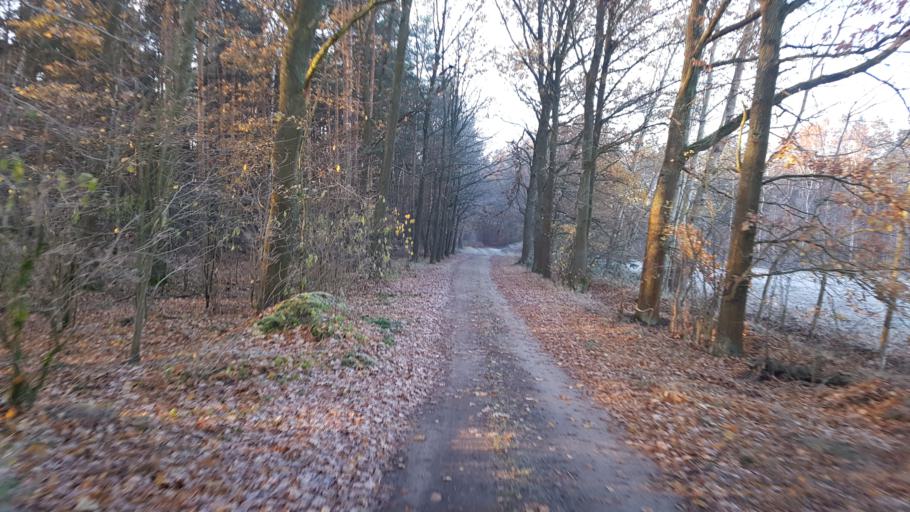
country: DE
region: Brandenburg
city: Sallgast
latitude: 51.6058
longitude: 13.8363
